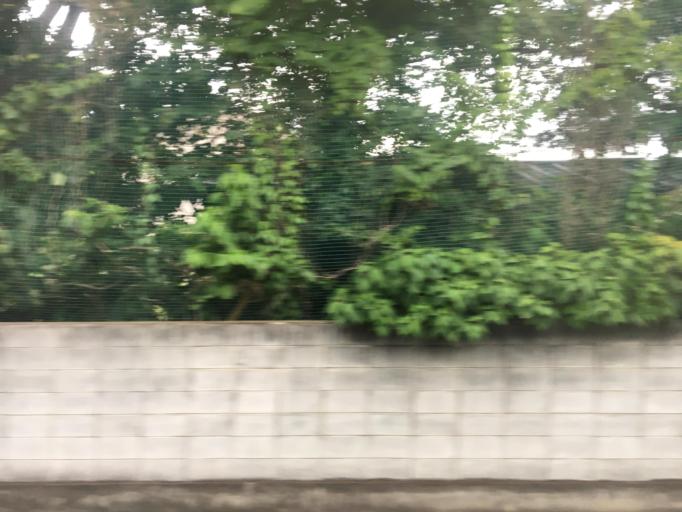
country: JP
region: Gunma
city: Maebashi-shi
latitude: 36.3901
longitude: 139.0804
